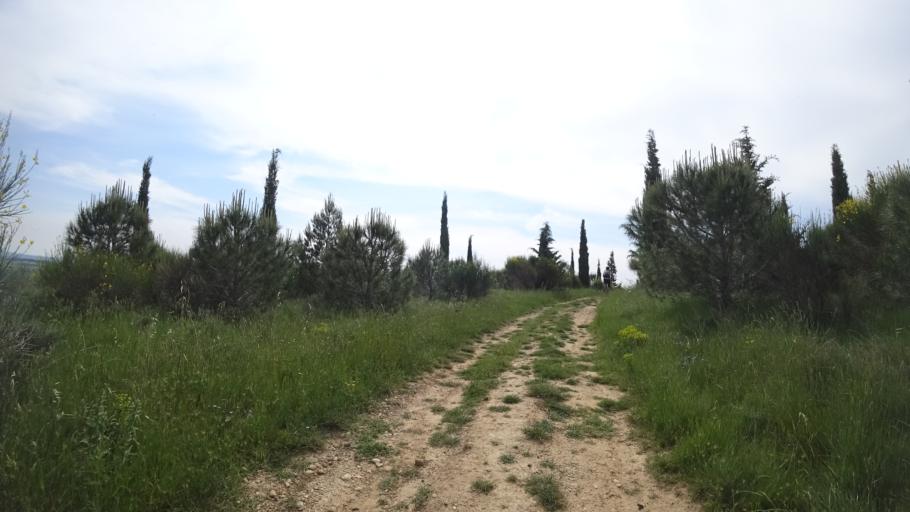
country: FR
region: Languedoc-Roussillon
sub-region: Departement de l'Aude
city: Canet
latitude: 43.2590
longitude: 2.8075
